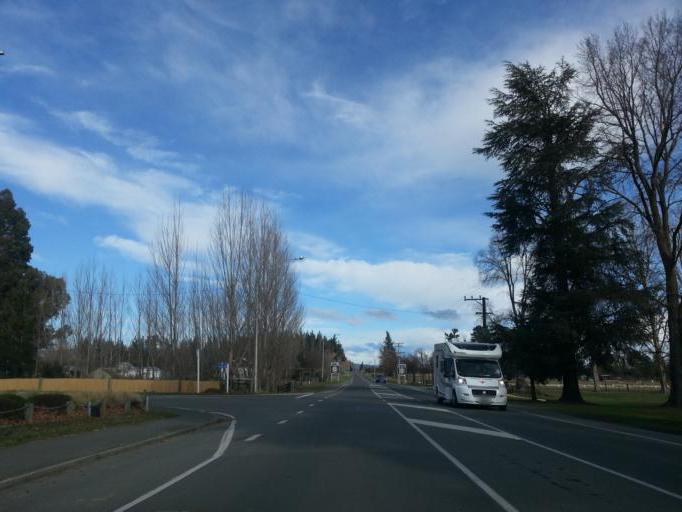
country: NZ
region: Canterbury
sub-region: Hurunui District
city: Amberley
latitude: -42.7757
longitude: 172.8468
